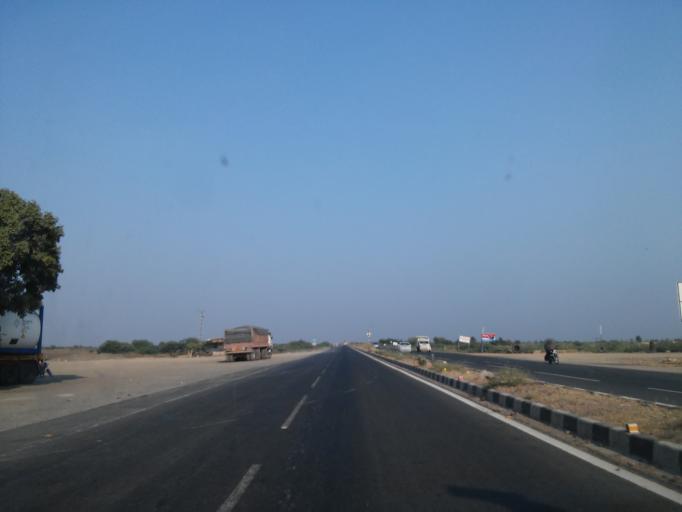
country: IN
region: Gujarat
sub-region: Surendranagar
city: Dhrangadhra
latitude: 23.0297
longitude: 71.6534
